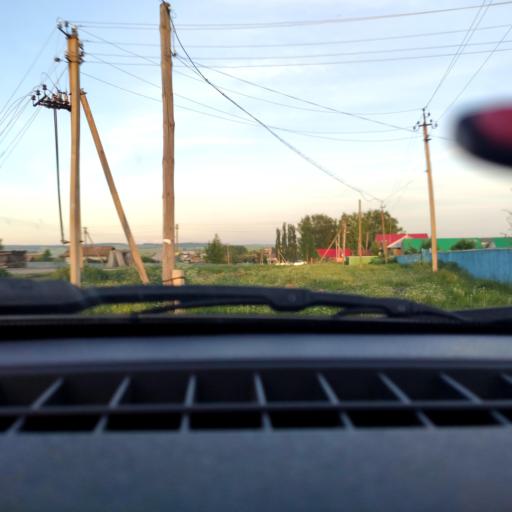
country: RU
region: Bashkortostan
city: Tolbazy
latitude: 54.2956
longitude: 55.8161
